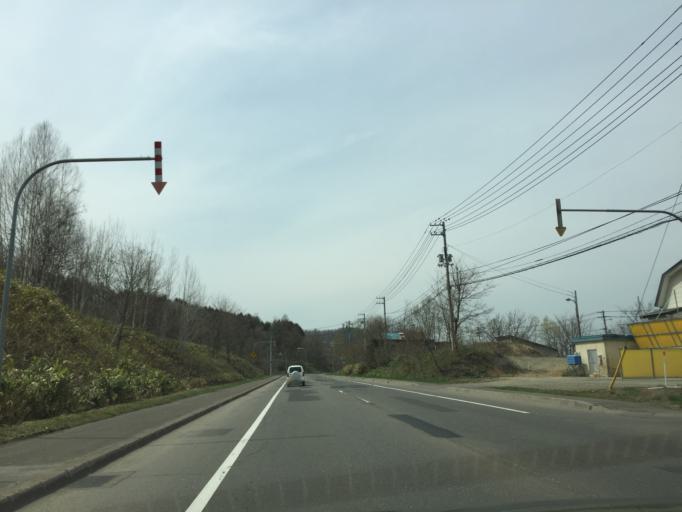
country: JP
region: Hokkaido
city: Akabira
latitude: 43.5392
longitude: 142.0743
